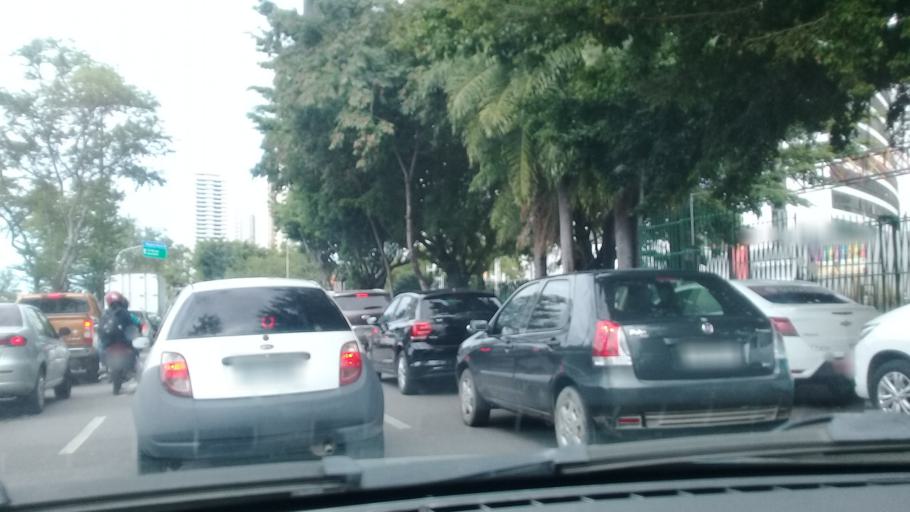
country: BR
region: Pernambuco
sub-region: Recife
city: Recife
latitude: -8.1173
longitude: -34.9052
